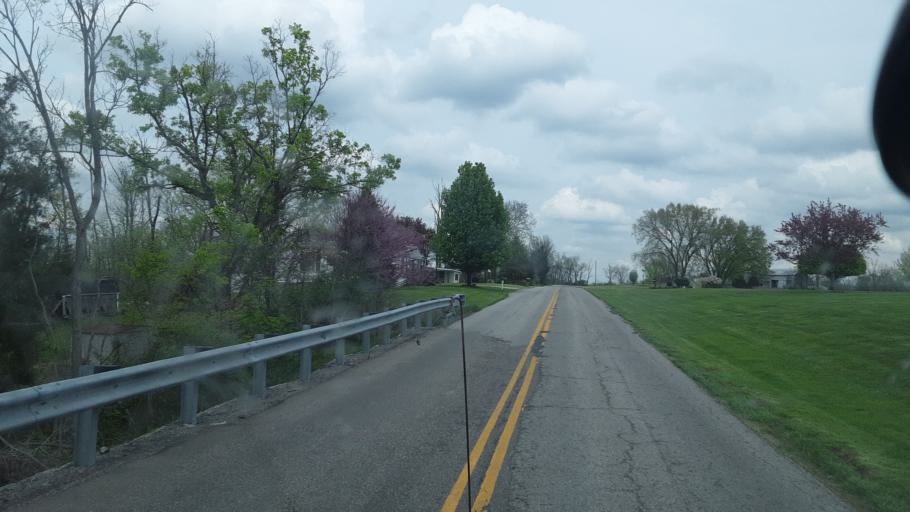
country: US
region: Kentucky
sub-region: Grant County
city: Dry Ridge
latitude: 38.6587
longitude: -84.7005
